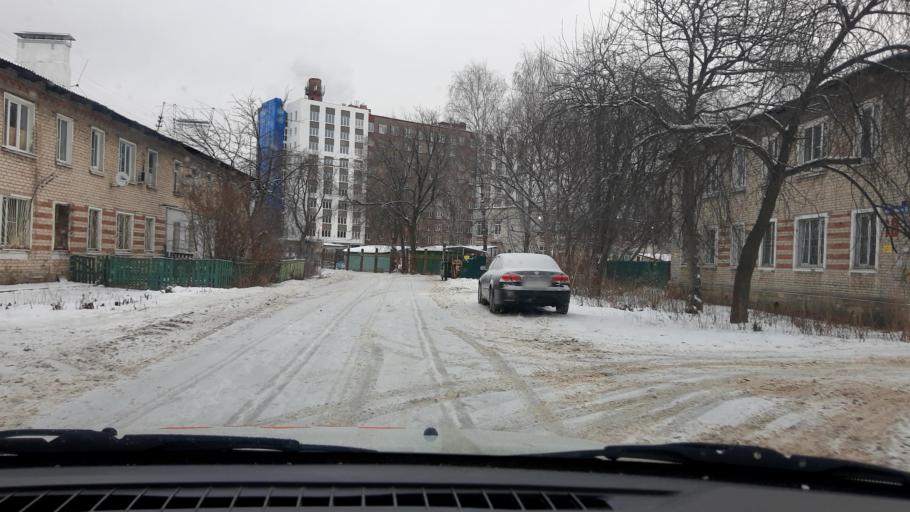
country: RU
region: Nizjnij Novgorod
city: Nizhniy Novgorod
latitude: 56.2766
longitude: 43.9443
